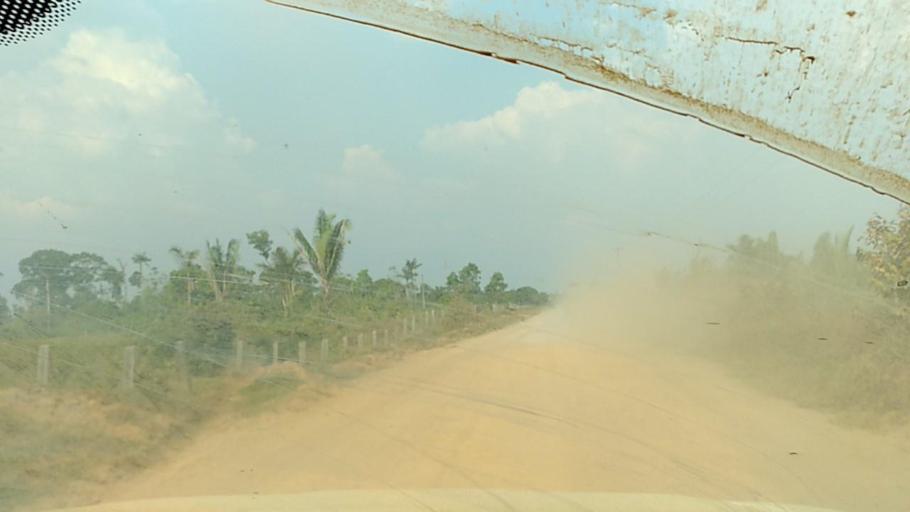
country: BR
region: Rondonia
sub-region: Porto Velho
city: Porto Velho
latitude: -8.6830
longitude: -63.1940
